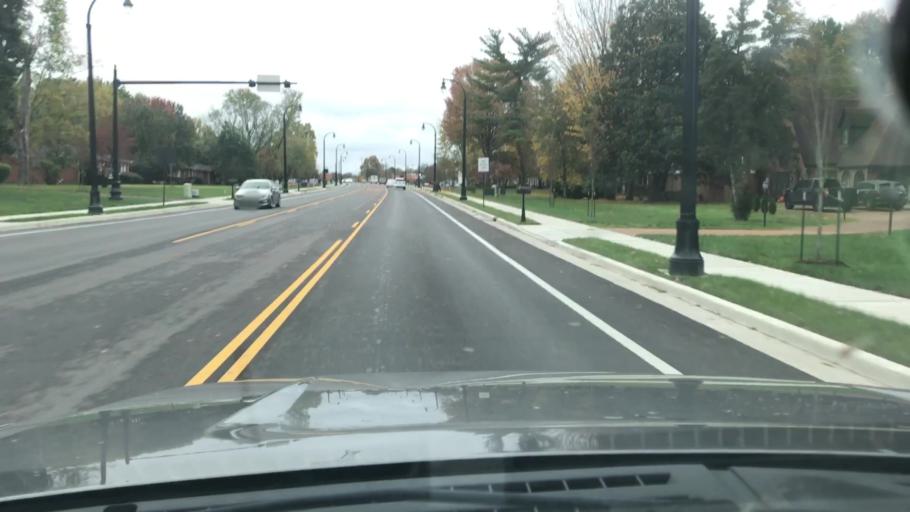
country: US
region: Tennessee
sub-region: Williamson County
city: Franklin
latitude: 35.9368
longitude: -86.8787
